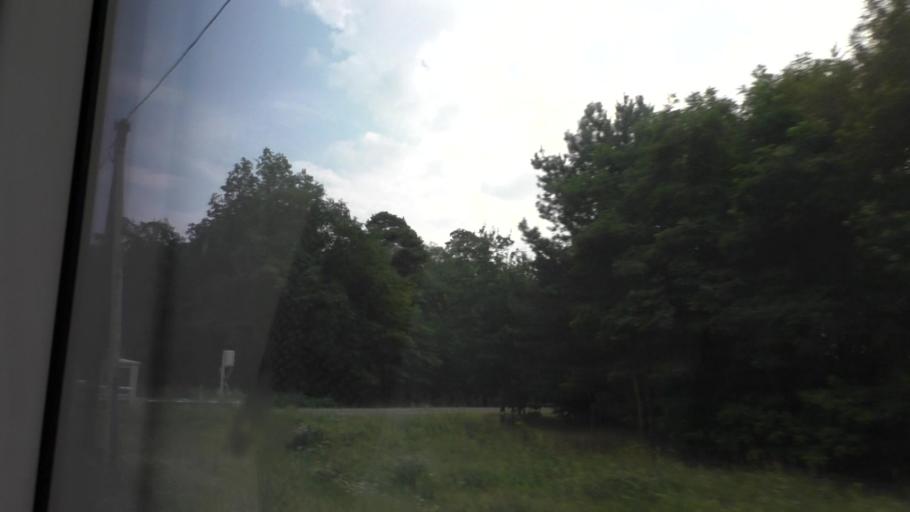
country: DE
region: Brandenburg
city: Storkow
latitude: 52.2647
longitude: 13.8947
